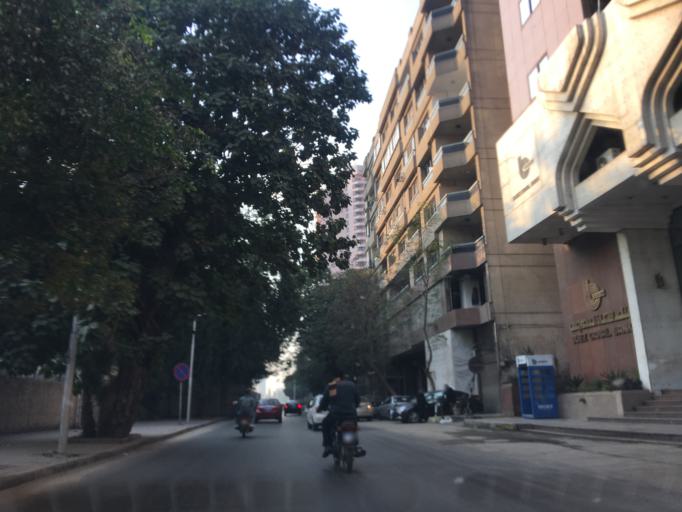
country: EG
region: Muhafazat al Qahirah
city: Cairo
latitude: 30.0419
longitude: 31.2344
